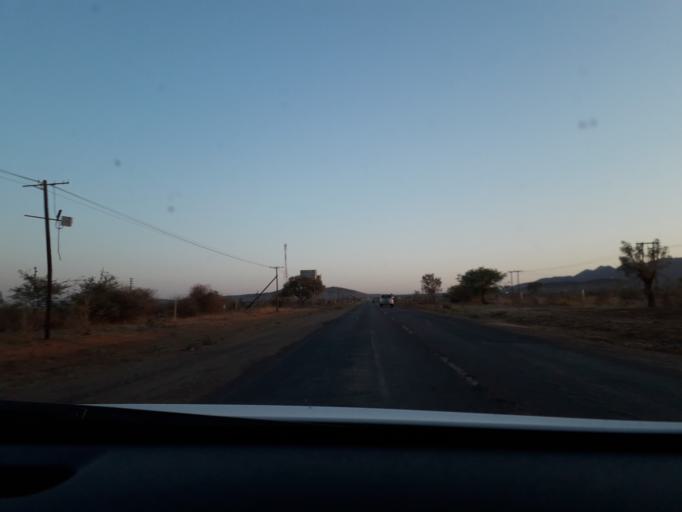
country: ZA
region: Limpopo
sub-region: Waterberg District Municipality
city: Mokopane
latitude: -24.0996
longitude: 28.9681
